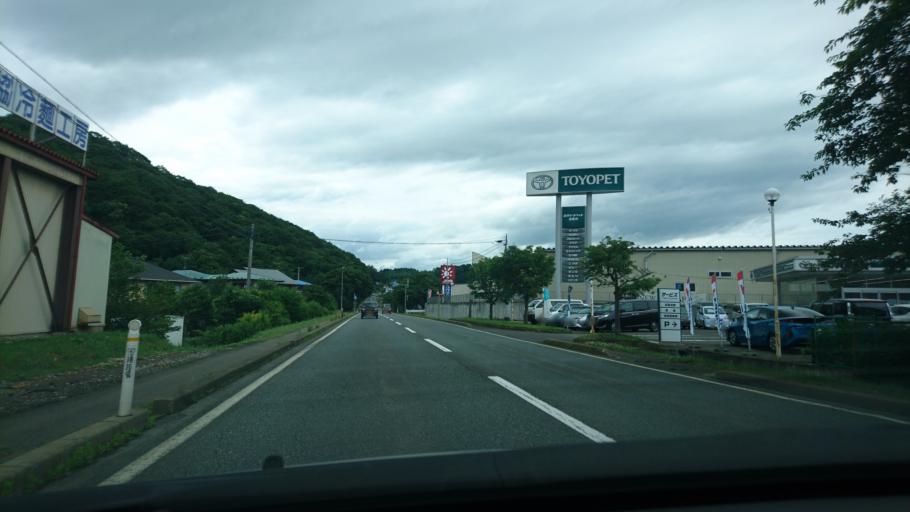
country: JP
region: Iwate
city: Morioka-shi
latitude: 39.9522
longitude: 141.2159
